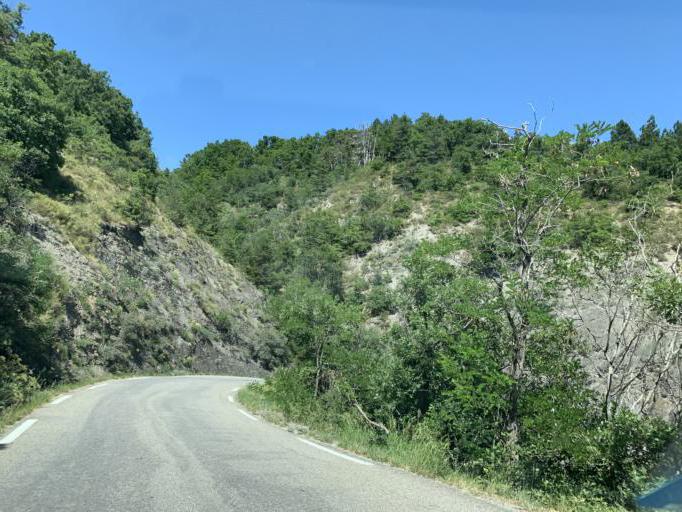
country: FR
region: Provence-Alpes-Cote d'Azur
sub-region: Departement des Hautes-Alpes
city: La Batie-Neuve
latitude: 44.5866
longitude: 6.1618
